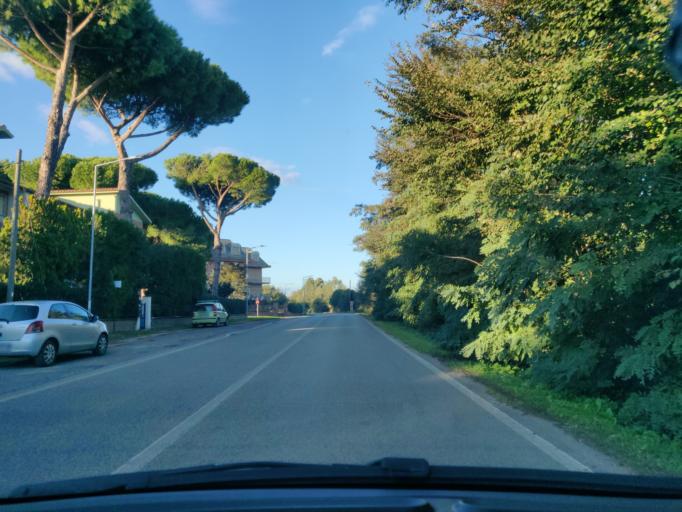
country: IT
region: Latium
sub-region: Provincia di Viterbo
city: Tarquinia
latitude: 42.2214
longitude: 11.7160
